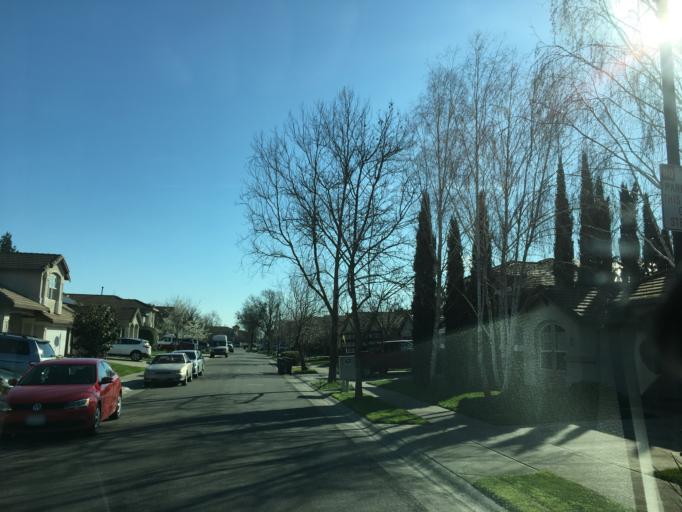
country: US
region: California
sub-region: Yolo County
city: Davis
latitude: 38.5575
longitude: -121.7015
